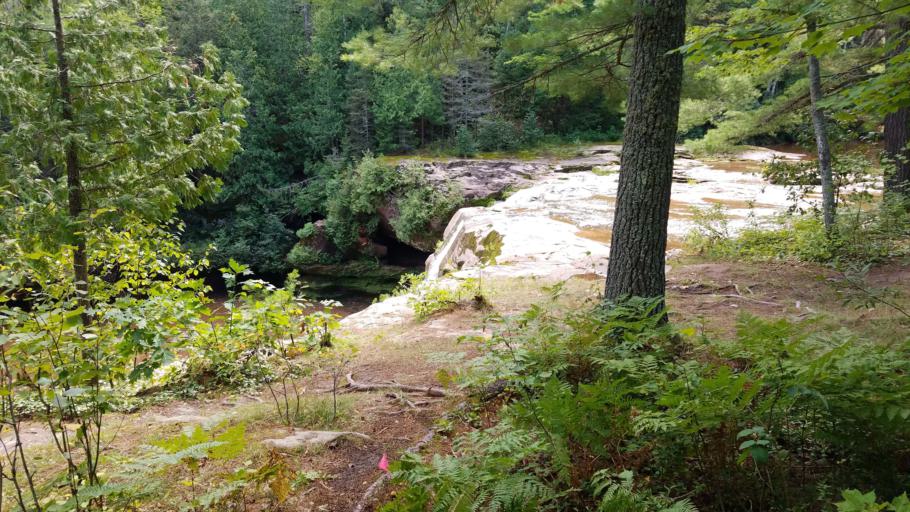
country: US
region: Michigan
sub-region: Ontonagon County
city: Ontonagon
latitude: 46.6516
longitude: -89.1525
